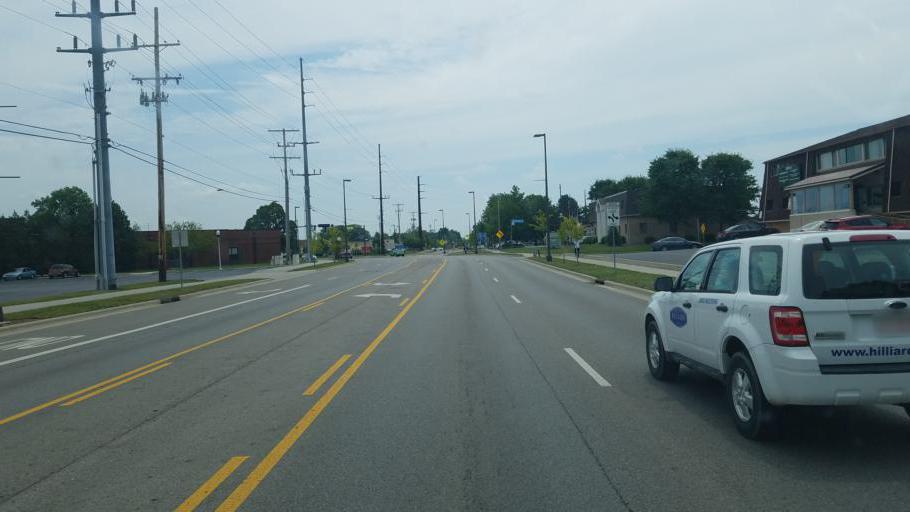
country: US
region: Ohio
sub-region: Franklin County
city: Hilliard
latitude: 40.0302
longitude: -83.1642
